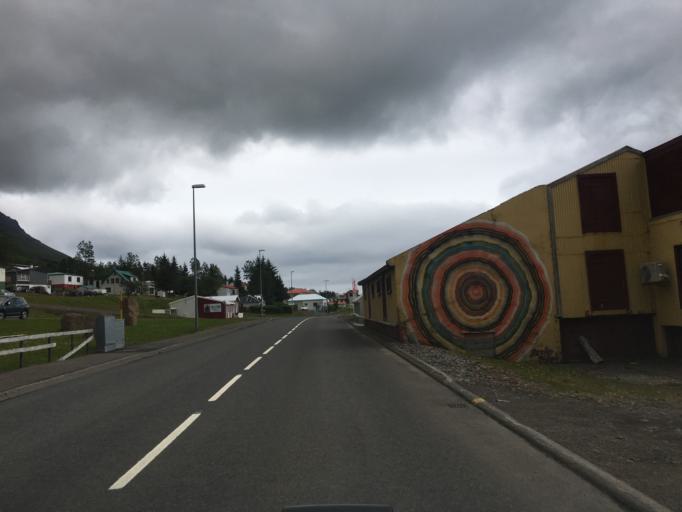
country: IS
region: East
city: Neskaupstadur
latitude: 65.1474
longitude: -13.7094
